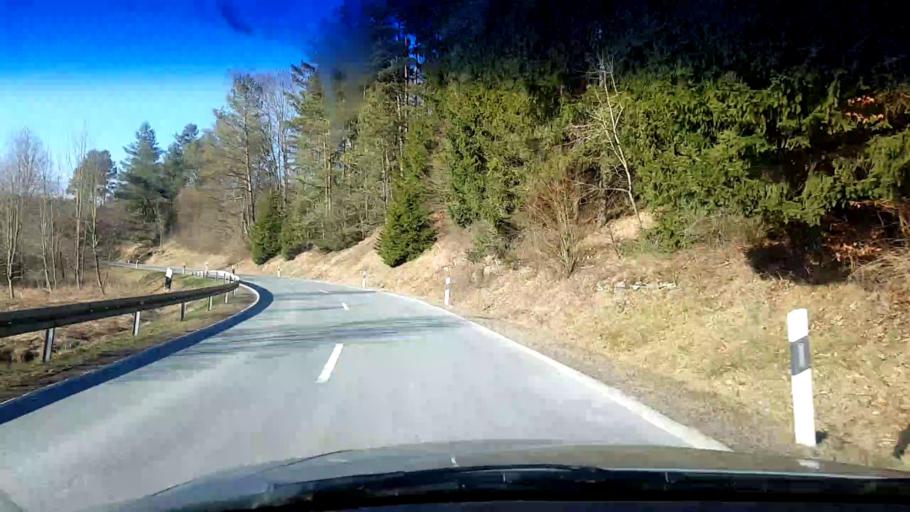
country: DE
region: Bavaria
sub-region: Upper Franconia
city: Aufsess
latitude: 49.8921
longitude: 11.2264
